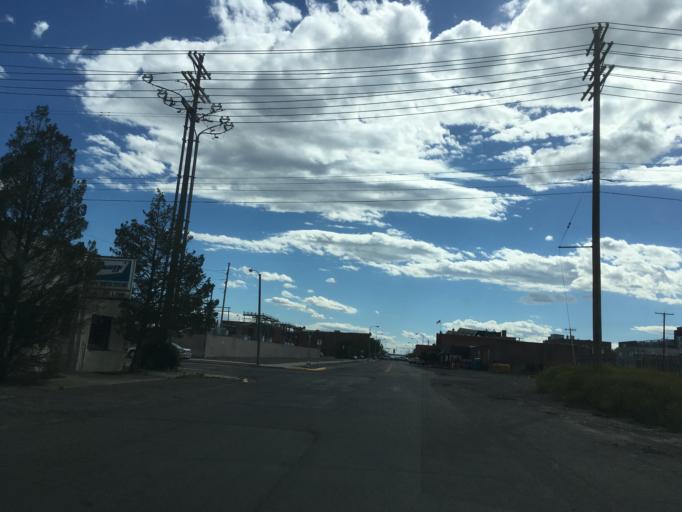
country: US
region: Montana
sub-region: Yellowstone County
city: Billings
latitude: 45.7824
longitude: -108.4999
